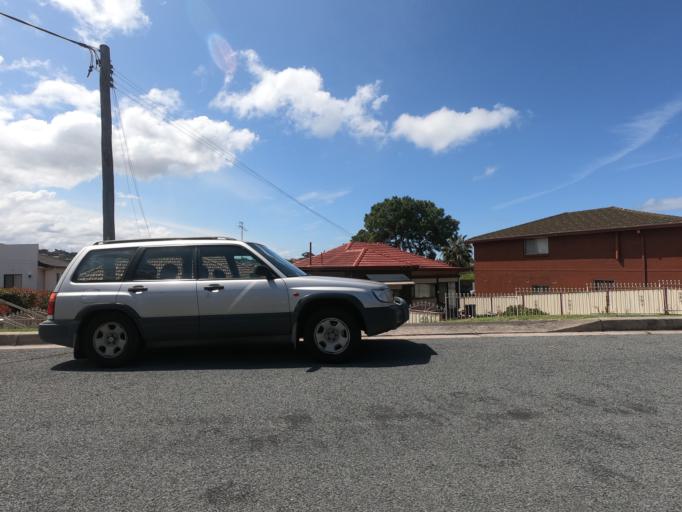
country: AU
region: New South Wales
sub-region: Wollongong
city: Lake Heights
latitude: -34.4882
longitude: 150.8707
